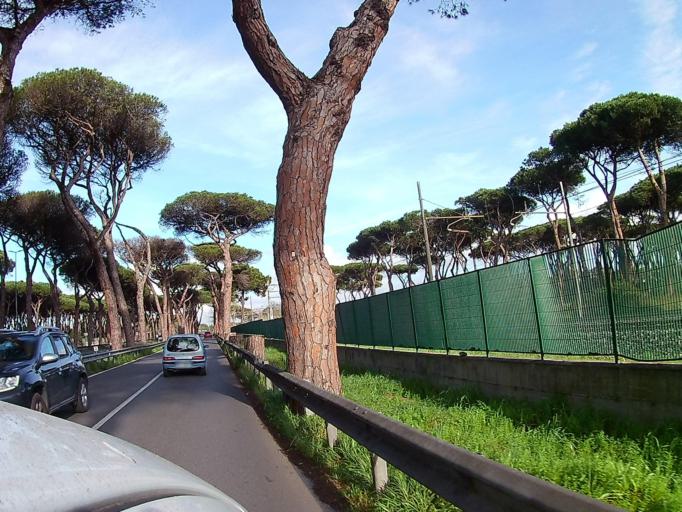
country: IT
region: Latium
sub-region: Citta metropolitana di Roma Capitale
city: Lido di Ostia
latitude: 41.7450
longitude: 12.2877
